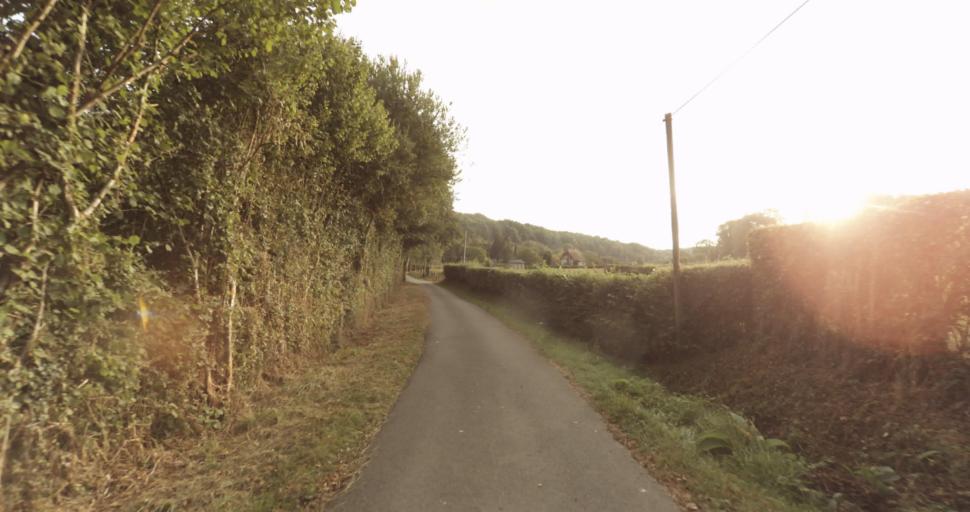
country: FR
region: Lower Normandy
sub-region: Departement de l'Orne
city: Vimoutiers
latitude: 48.9448
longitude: 0.2113
